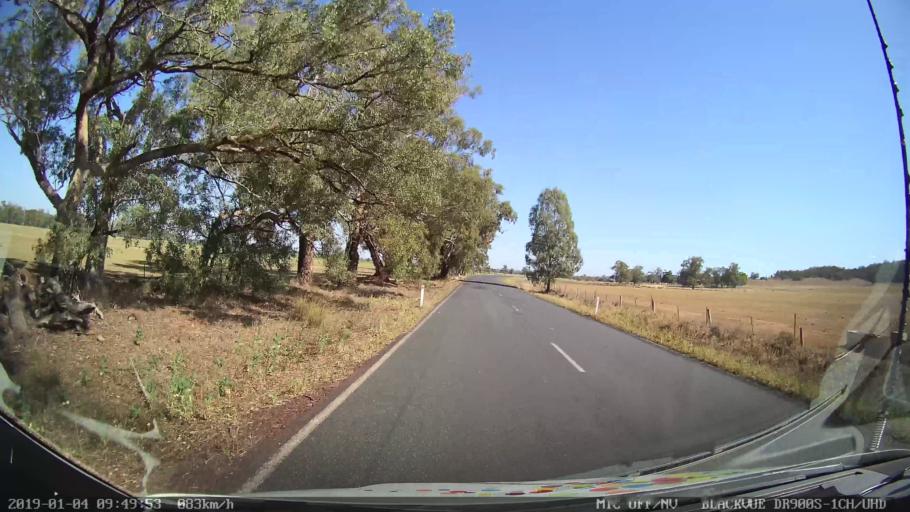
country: AU
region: New South Wales
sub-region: Cabonne
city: Canowindra
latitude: -33.5907
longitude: 148.4155
